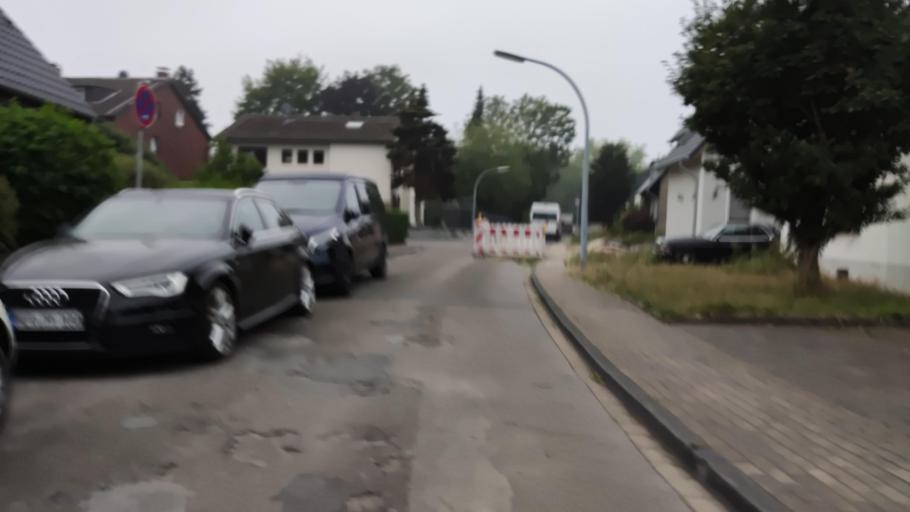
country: DE
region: North Rhine-Westphalia
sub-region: Regierungsbezirk Arnsberg
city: Herne
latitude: 51.5350
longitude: 7.2358
